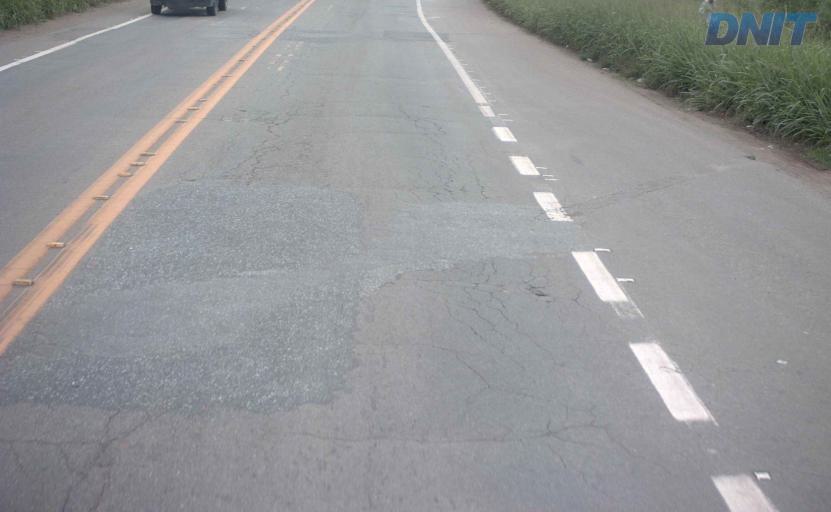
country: BR
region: Minas Gerais
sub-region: Barao De Cocais
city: Barao de Cocais
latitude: -19.8351
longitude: -43.3495
